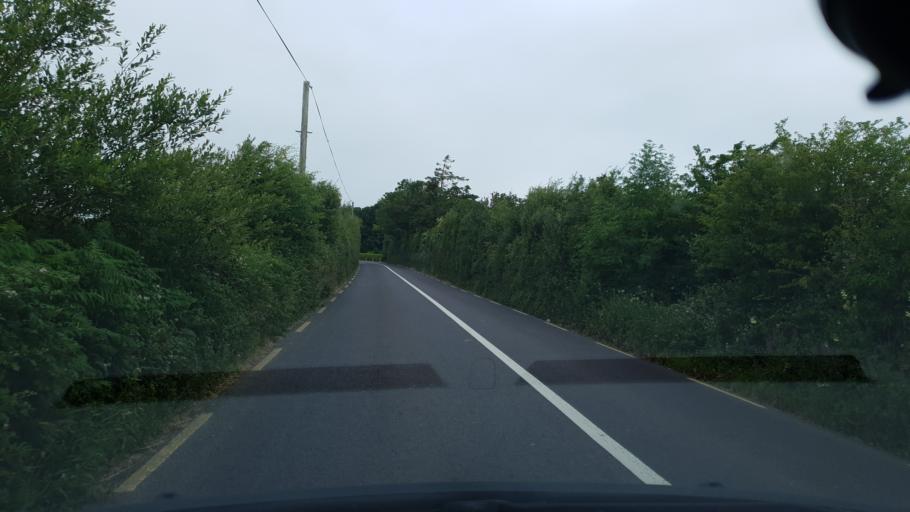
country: IE
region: Munster
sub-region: Ciarrai
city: Tralee
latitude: 52.1603
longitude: -9.6860
